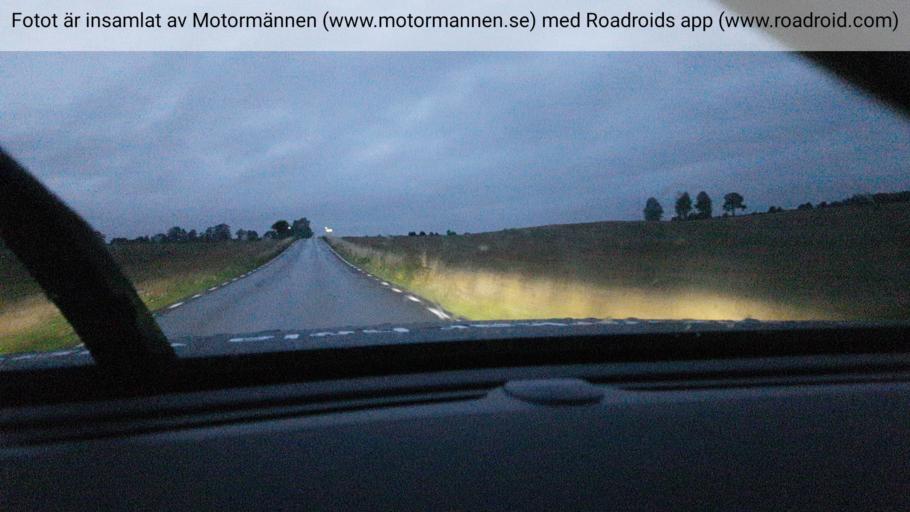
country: SE
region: Vaestra Goetaland
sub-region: Tidaholms Kommun
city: Tidaholm
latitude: 58.2007
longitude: 13.8256
